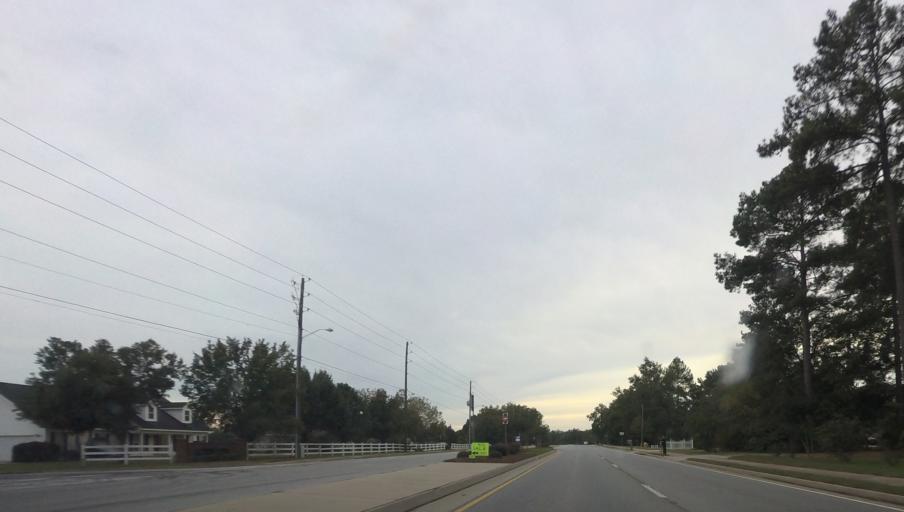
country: US
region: Georgia
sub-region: Houston County
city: Centerville
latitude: 32.5343
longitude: -83.6611
